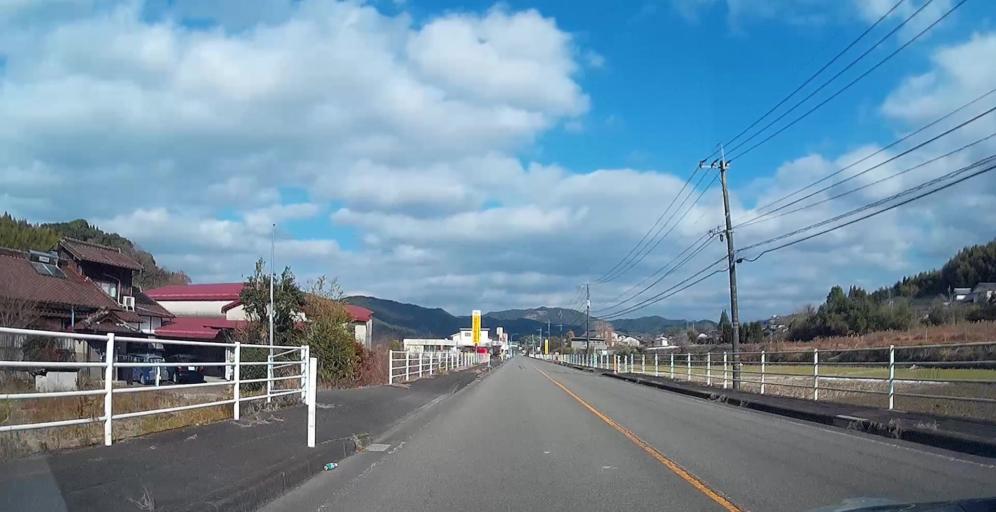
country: JP
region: Kumamoto
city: Yatsushiro
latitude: 32.3966
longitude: 130.5490
